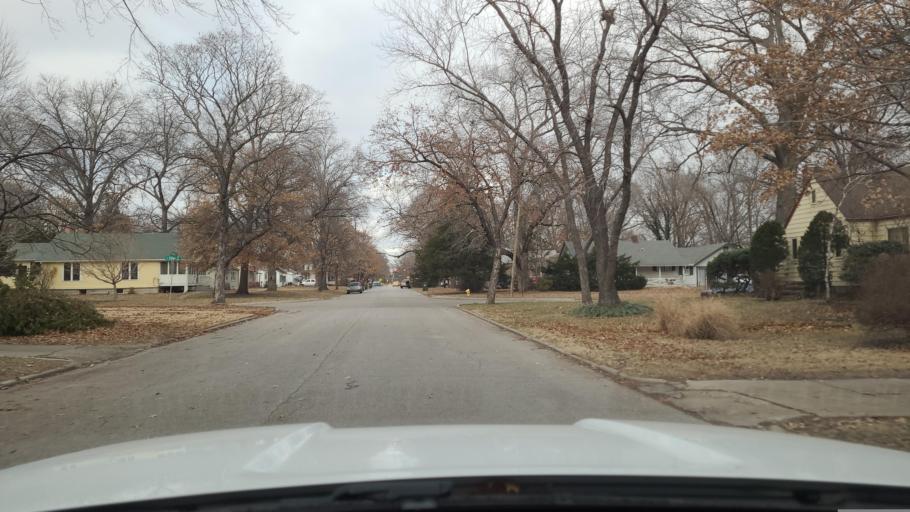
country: US
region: Kansas
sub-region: Douglas County
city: Lawrence
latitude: 38.9477
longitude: -95.2382
